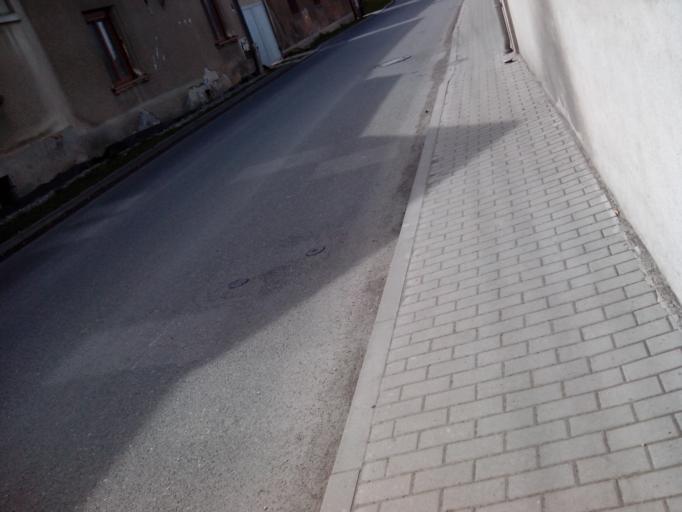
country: CZ
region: Central Bohemia
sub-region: Okres Beroun
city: Beroun
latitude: 49.9502
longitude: 14.0996
